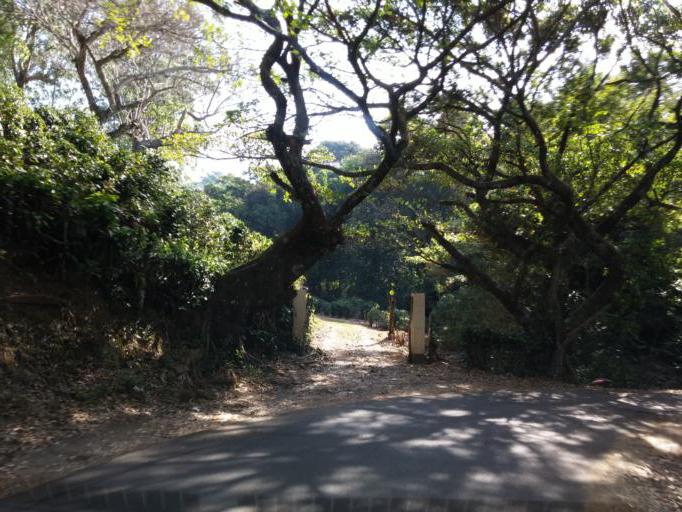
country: CR
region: Alajuela
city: Sabanilla
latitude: 10.0795
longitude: -84.1849
